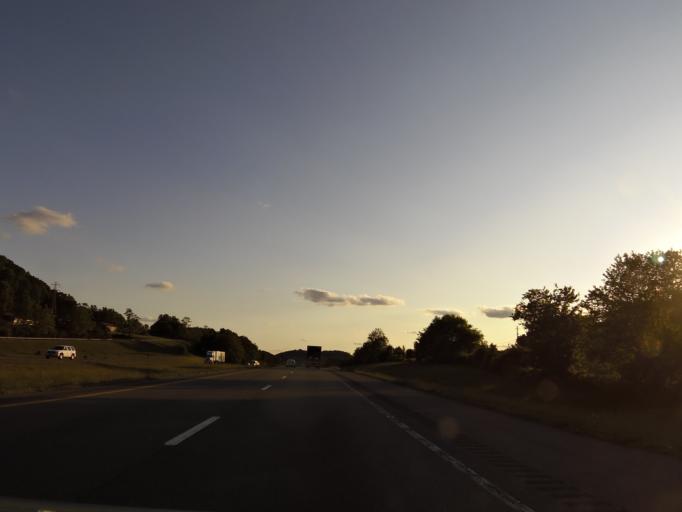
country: US
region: Tennessee
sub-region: Sullivan County
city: Walnut Hill
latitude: 36.5676
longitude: -82.3000
